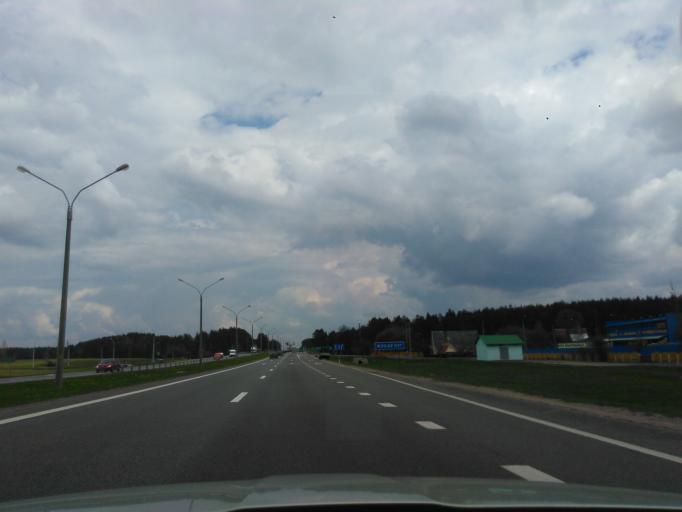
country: BY
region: Minsk
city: Korolev Stan
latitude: 53.9752
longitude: 27.7643
